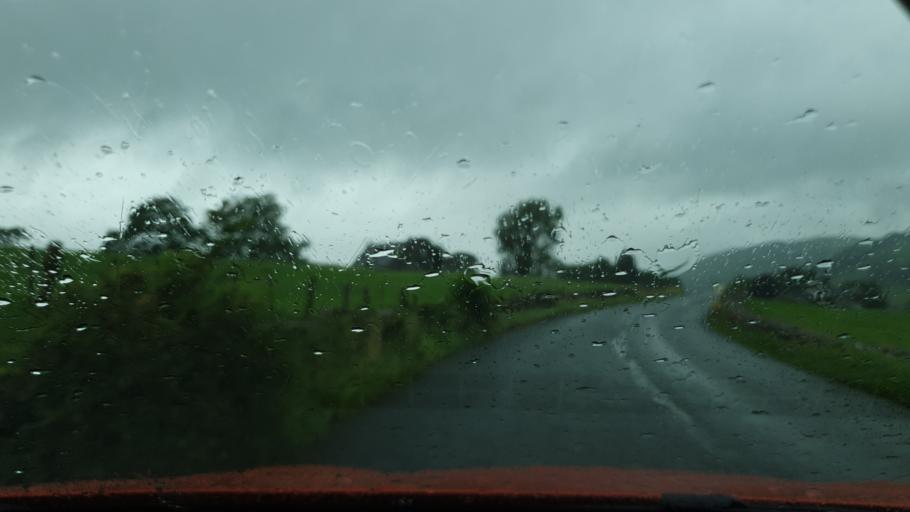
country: GB
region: England
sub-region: Cumbria
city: Ulverston
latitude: 54.2527
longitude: -3.0716
